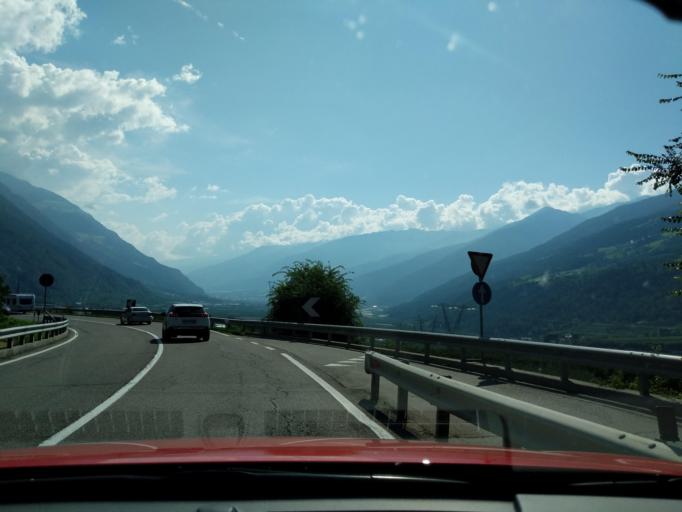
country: IT
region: Trentino-Alto Adige
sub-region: Bolzano
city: Silandro
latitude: 46.6244
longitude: 10.7552
